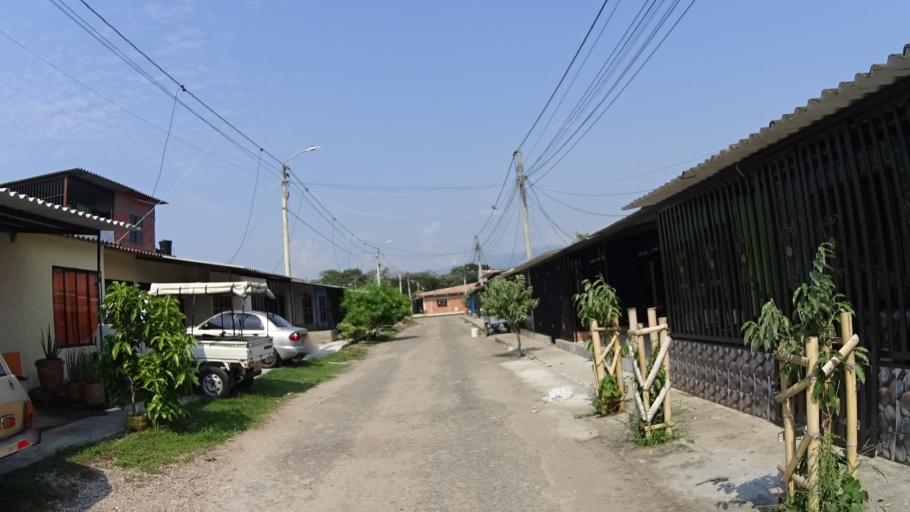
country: CO
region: Cundinamarca
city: Puerto Salgar
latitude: 5.4870
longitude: -74.6738
